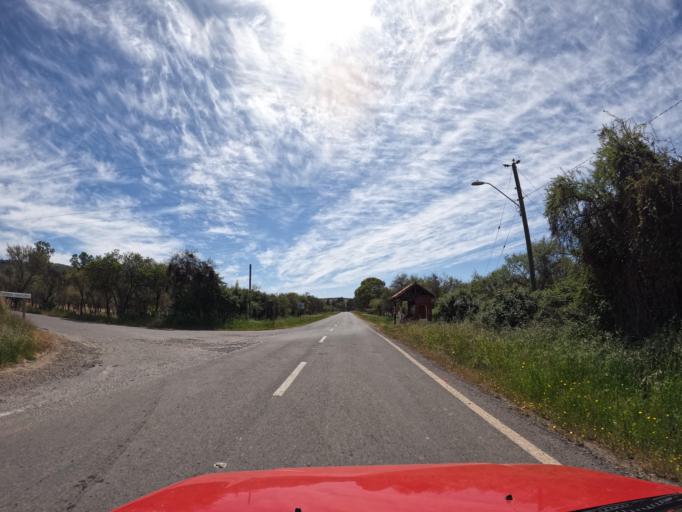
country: CL
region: Maule
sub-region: Provincia de Talca
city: Talca
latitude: -35.0283
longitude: -71.7654
